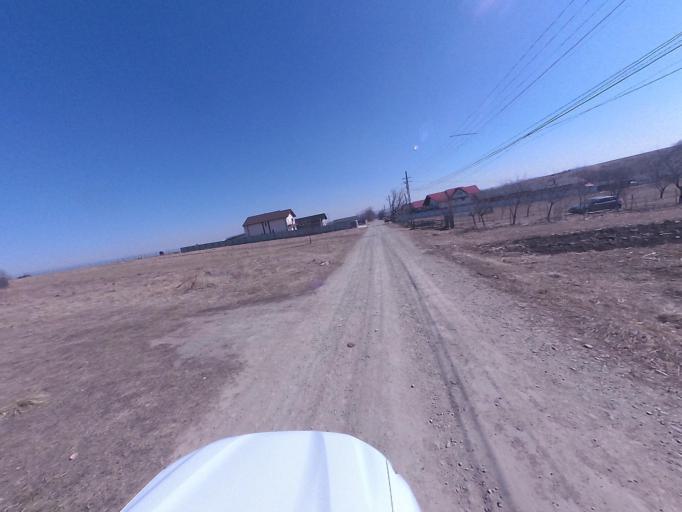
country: RO
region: Neamt
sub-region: Oras Targu Neamt
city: Humulesti
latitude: 47.1871
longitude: 26.3393
